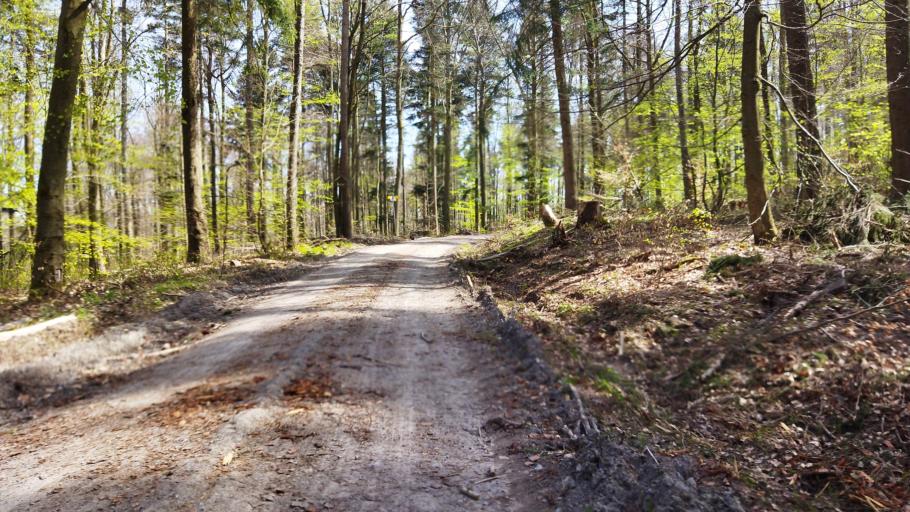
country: DE
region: Baden-Wuerttemberg
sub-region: Regierungsbezirk Stuttgart
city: Zaberfeld
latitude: 49.0347
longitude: 8.9345
